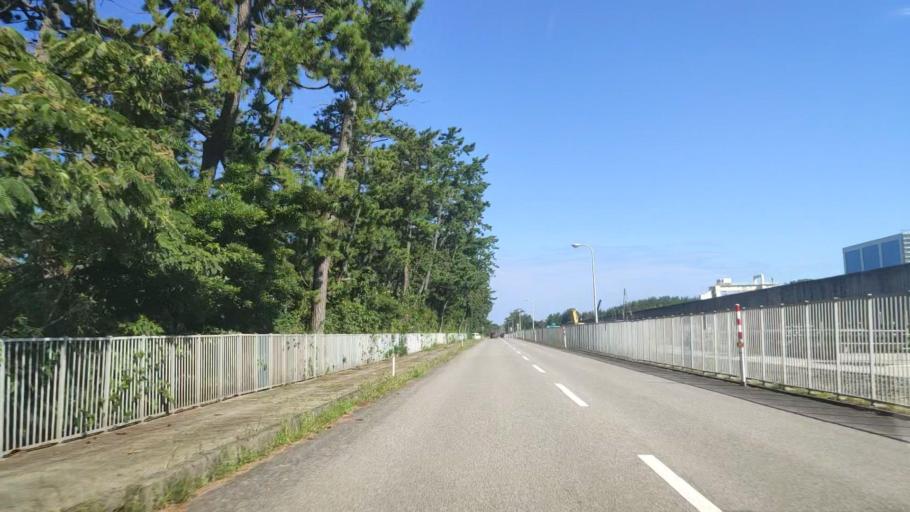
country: JP
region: Ishikawa
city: Hakui
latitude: 37.0588
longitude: 136.7237
